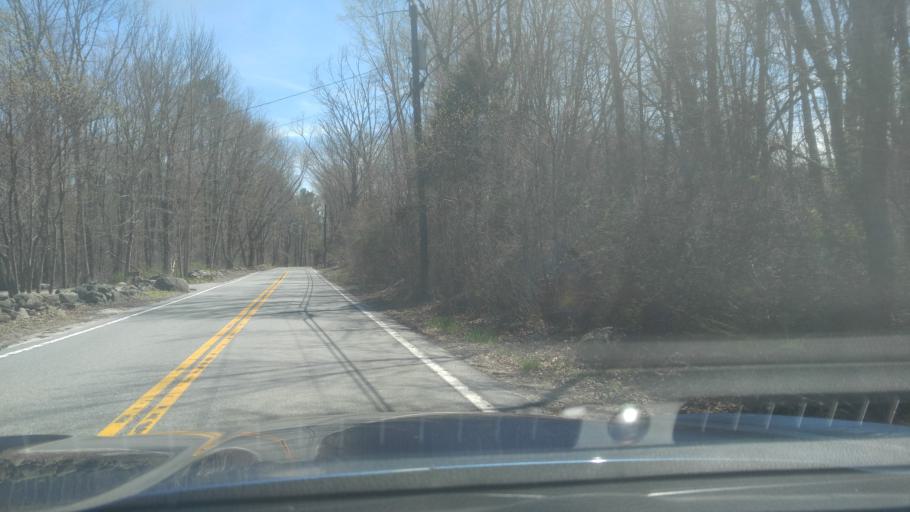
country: US
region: Rhode Island
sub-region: Washington County
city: Hope Valley
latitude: 41.5898
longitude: -71.7584
